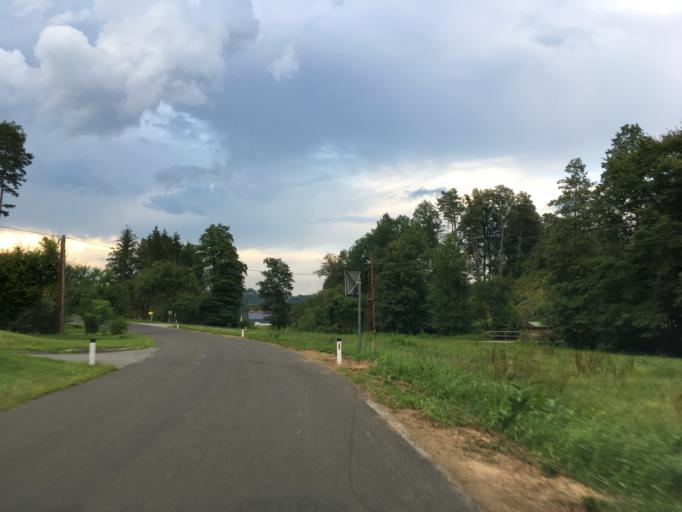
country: AT
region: Styria
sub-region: Politischer Bezirk Leibnitz
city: Oberhaag
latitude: 46.6774
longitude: 15.3526
